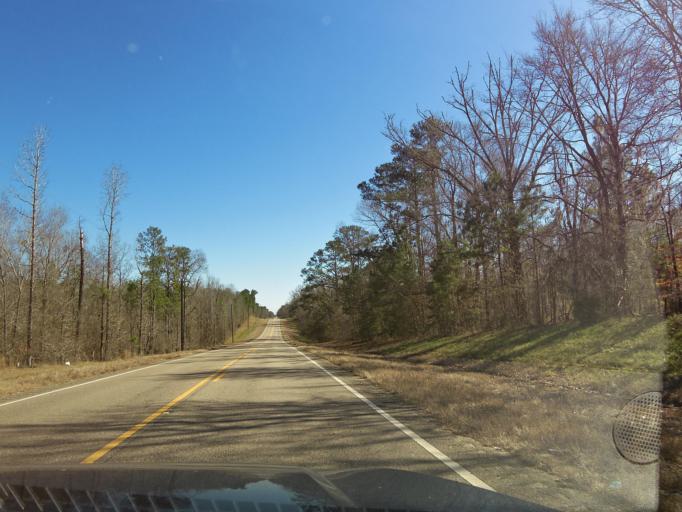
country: US
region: Alabama
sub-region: Montgomery County
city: Pike Road
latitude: 32.1899
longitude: -86.1106
